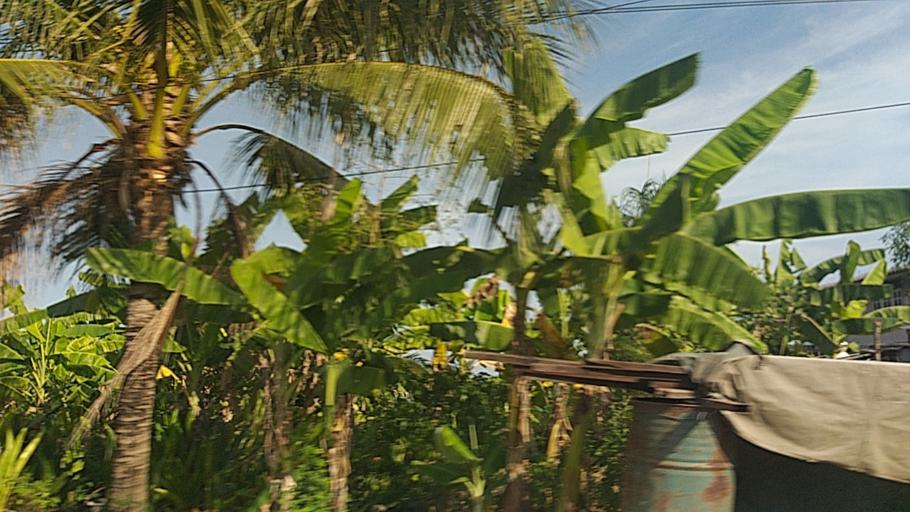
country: TH
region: Pathum Thani
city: Thanyaburi
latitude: 13.9893
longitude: 100.7300
